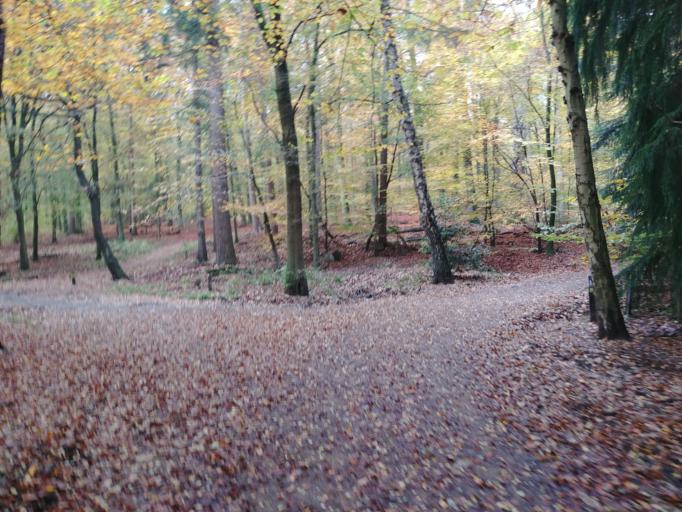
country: NL
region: Gelderland
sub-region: Gemeente Rheden
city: De Steeg
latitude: 52.0234
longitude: 6.0541
